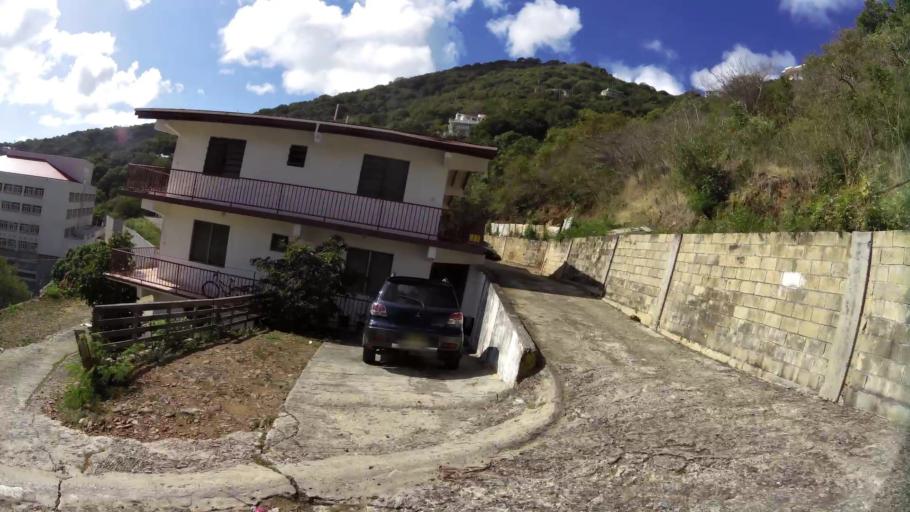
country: VG
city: Road Town
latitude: 18.4183
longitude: -64.6202
